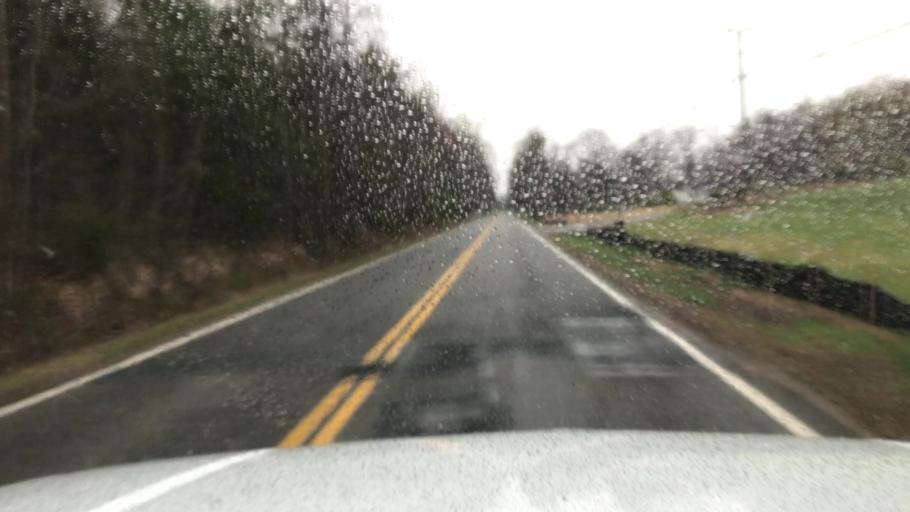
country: US
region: Virginia
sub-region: Henrico County
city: Short Pump
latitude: 37.6596
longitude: -77.6789
